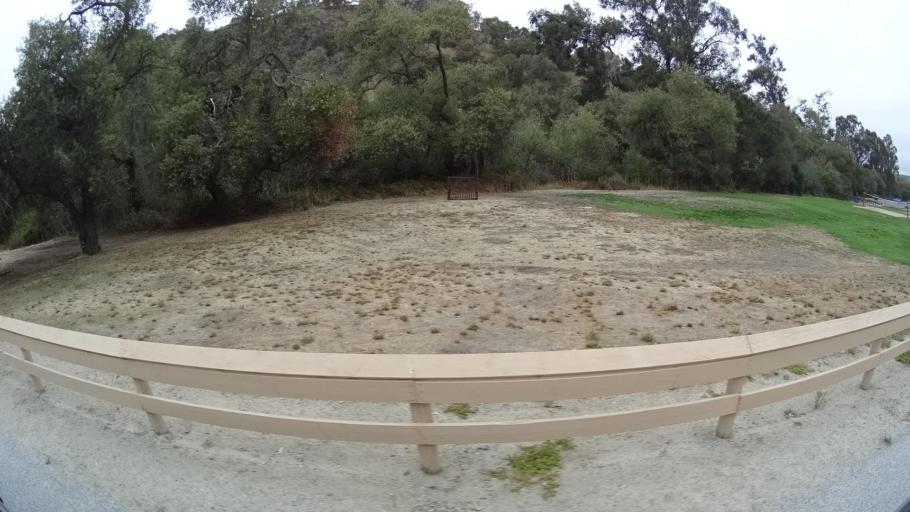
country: US
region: California
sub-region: Monterey County
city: Salinas
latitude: 36.5958
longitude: -121.6914
